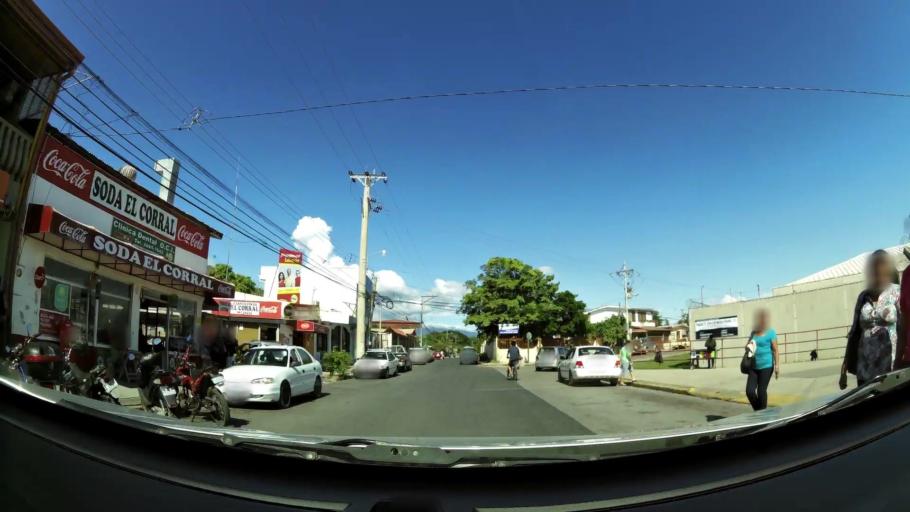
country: CR
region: Guanacaste
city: Liberia
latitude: 10.6398
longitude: -85.4314
